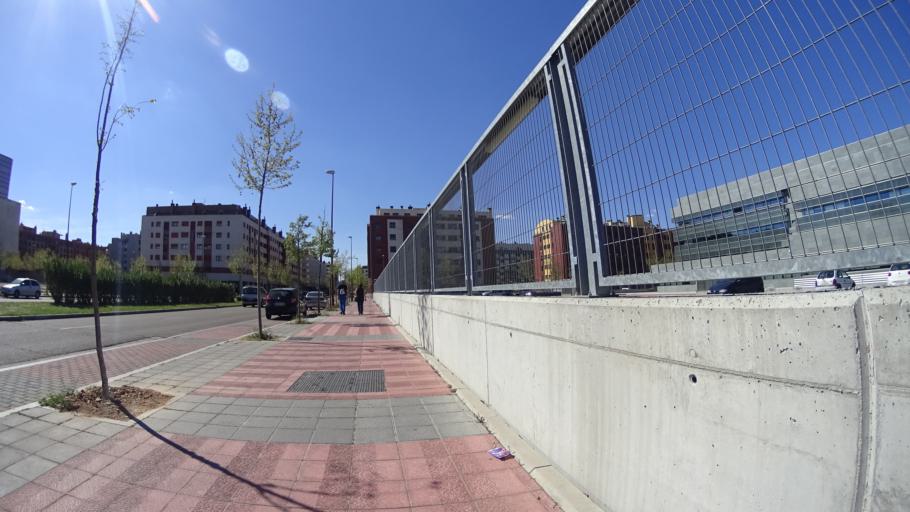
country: ES
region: Castille and Leon
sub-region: Provincia de Valladolid
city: Valladolid
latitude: 41.6449
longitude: -4.7436
